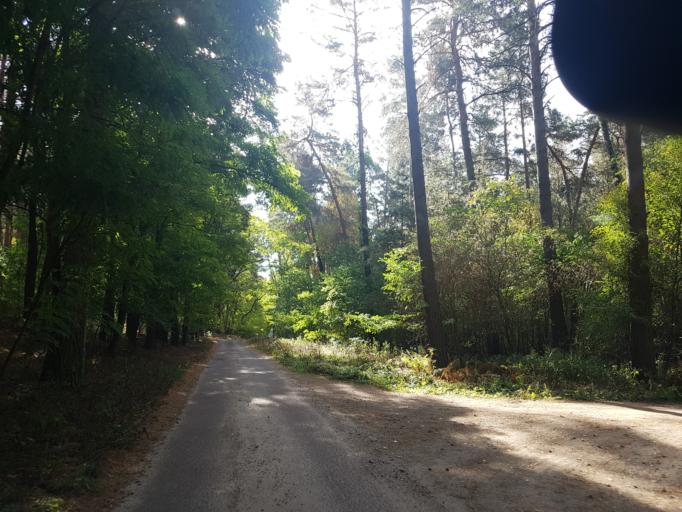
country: DE
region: Brandenburg
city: Belzig
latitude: 52.1517
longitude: 12.5774
